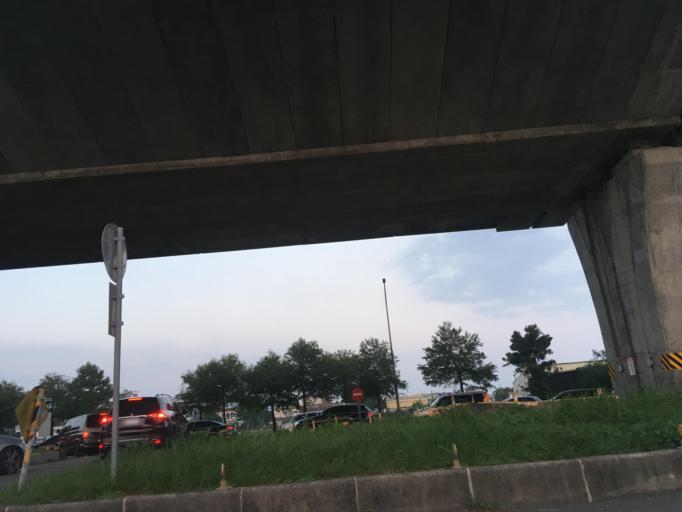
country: TW
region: Taiwan
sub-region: Yilan
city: Yilan
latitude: 24.6913
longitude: 121.7908
